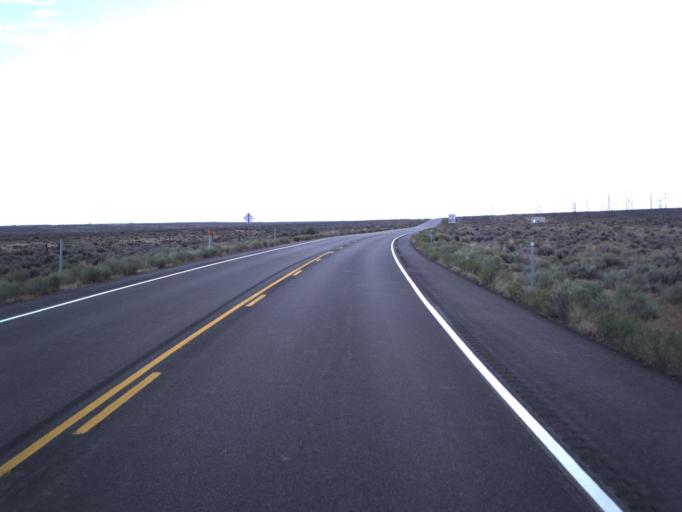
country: US
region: Utah
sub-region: Uintah County
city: Naples
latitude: 40.2202
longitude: -109.3865
